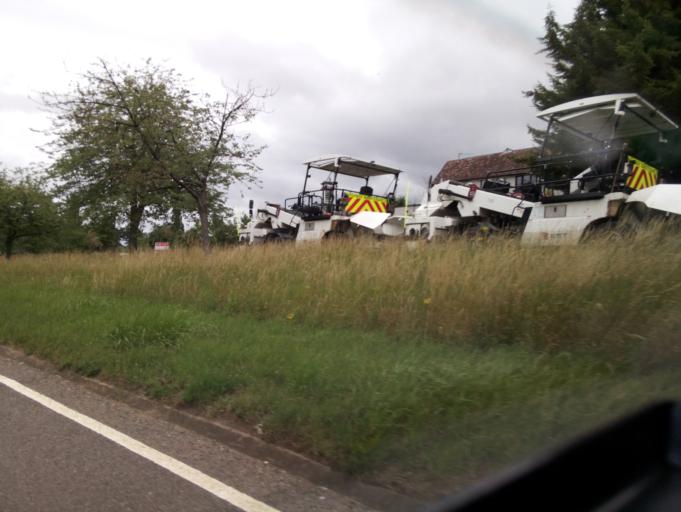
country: GB
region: England
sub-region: Worcestershire
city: Upton upon Severn
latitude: 52.0779
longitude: -2.2008
